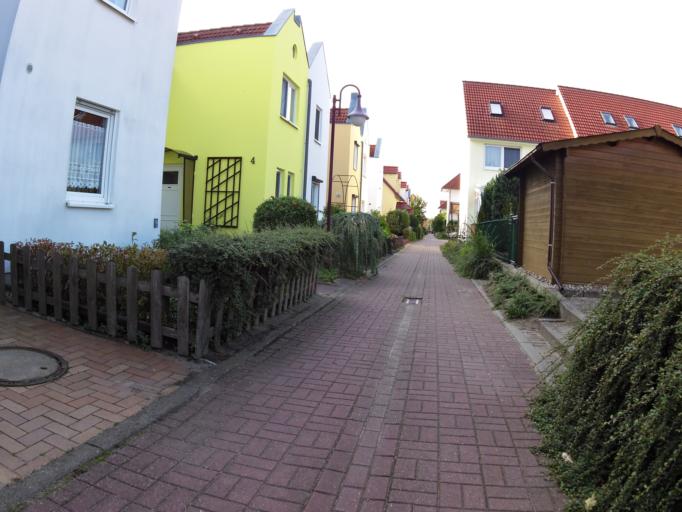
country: DE
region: Mecklenburg-Vorpommern
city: Seebad Heringsdorf
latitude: 53.9538
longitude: 14.1498
